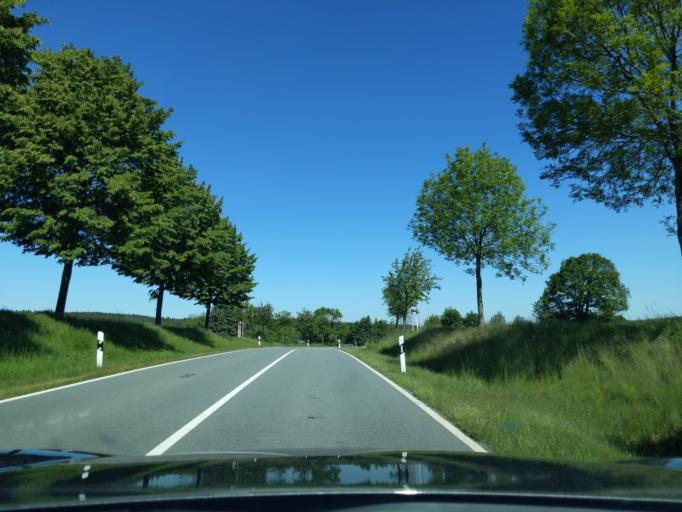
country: DE
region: Saxony
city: Stutzengrun
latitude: 50.5677
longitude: 12.4790
